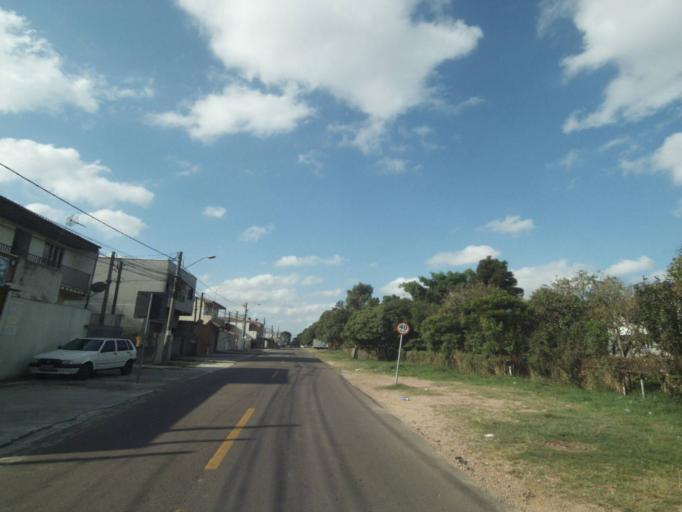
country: BR
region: Parana
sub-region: Curitiba
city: Curitiba
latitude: -25.5076
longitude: -49.3276
